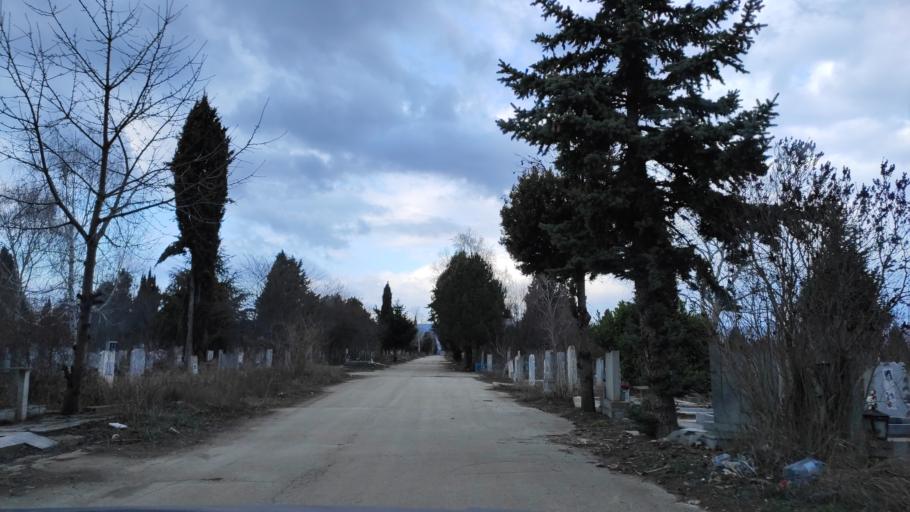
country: BG
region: Varna
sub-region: Obshtina Aksakovo
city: Aksakovo
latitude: 43.2184
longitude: 27.8090
